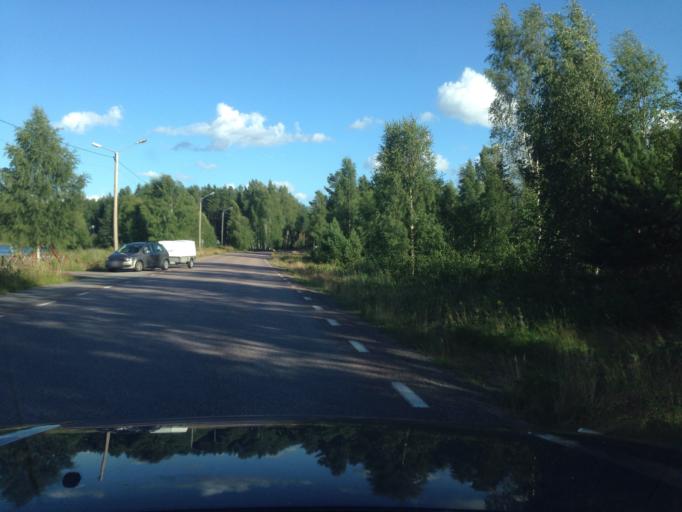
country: SE
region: Dalarna
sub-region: Ludvika Kommun
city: Grangesberg
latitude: 60.1529
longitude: 14.9757
